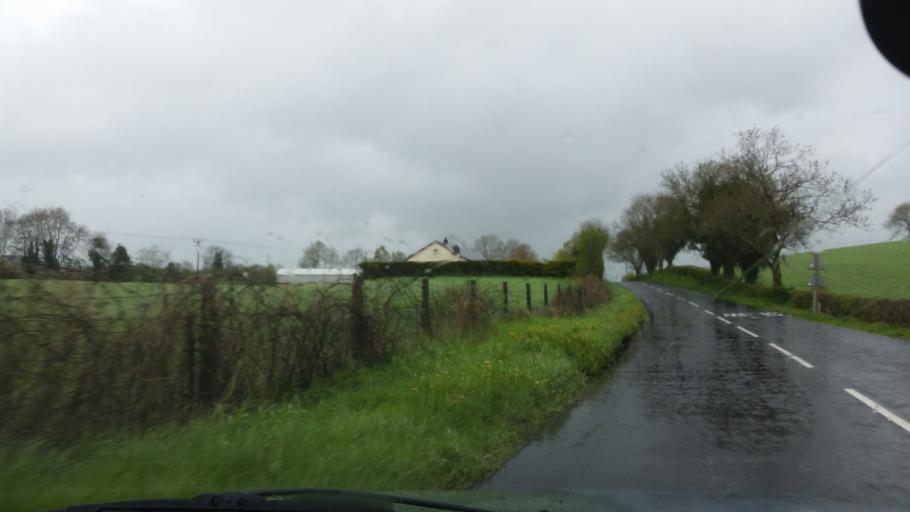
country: GB
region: Northern Ireland
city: Fintona
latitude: 54.5363
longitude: -7.2913
